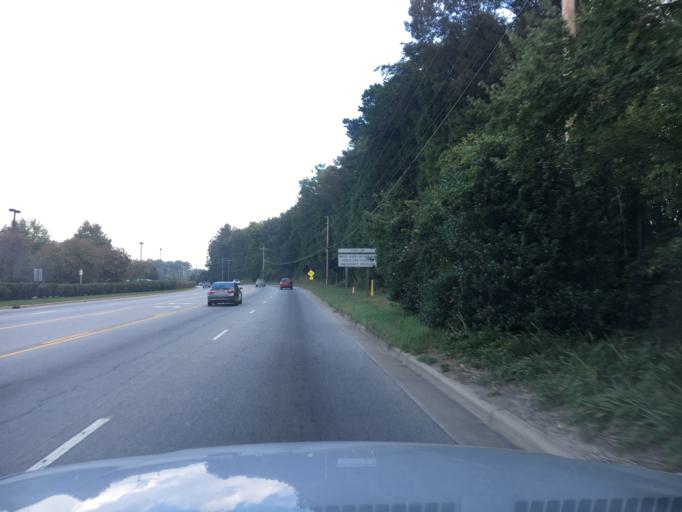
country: US
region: North Carolina
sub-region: Henderson County
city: Fletcher
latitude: 35.4319
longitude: -82.5348
